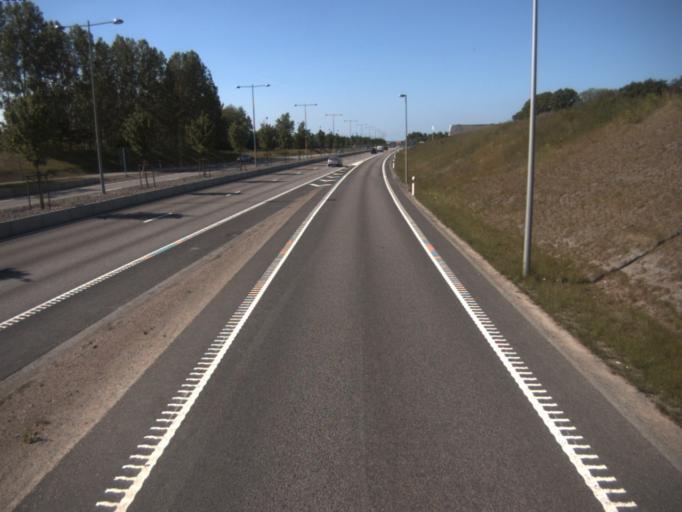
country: SE
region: Skane
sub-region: Helsingborg
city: Odakra
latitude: 56.0556
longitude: 12.7503
